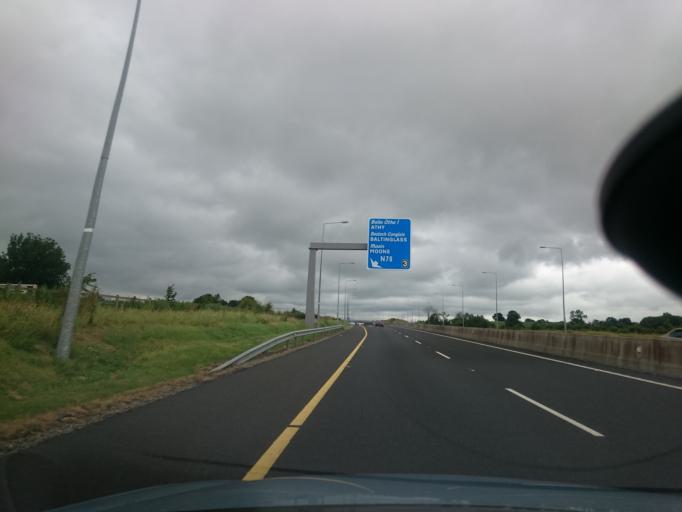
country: IE
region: Leinster
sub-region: Kildare
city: Moone
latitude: 52.9937
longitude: -6.8462
